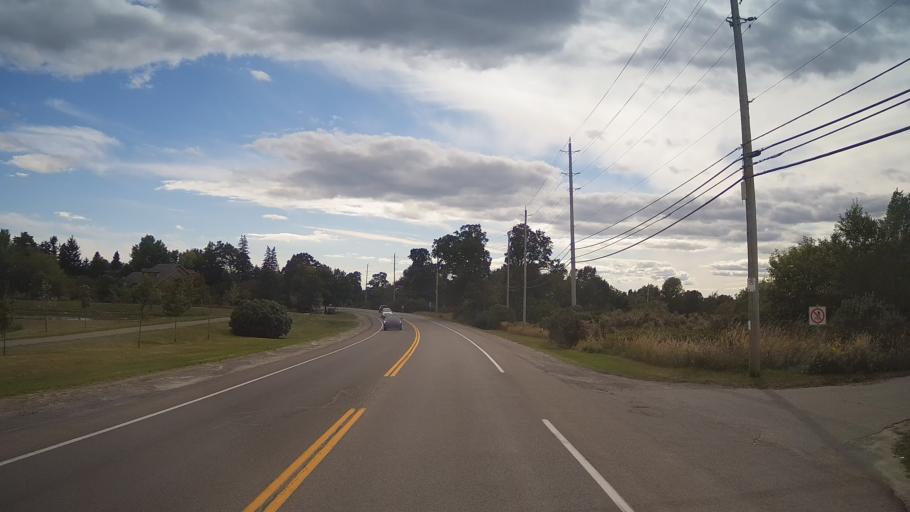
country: CA
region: Ontario
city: Kingston
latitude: 44.2632
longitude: -76.4580
